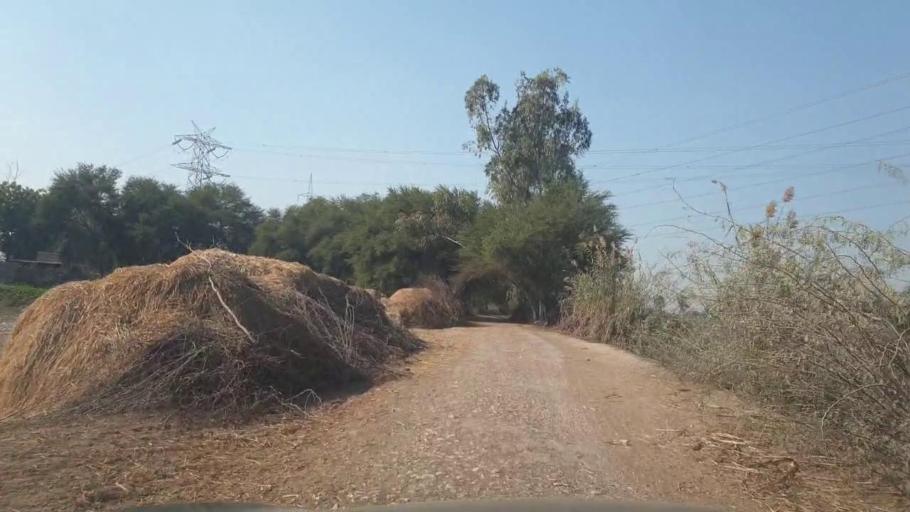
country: PK
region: Sindh
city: Mirpur Mathelo
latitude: 27.9875
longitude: 69.4721
